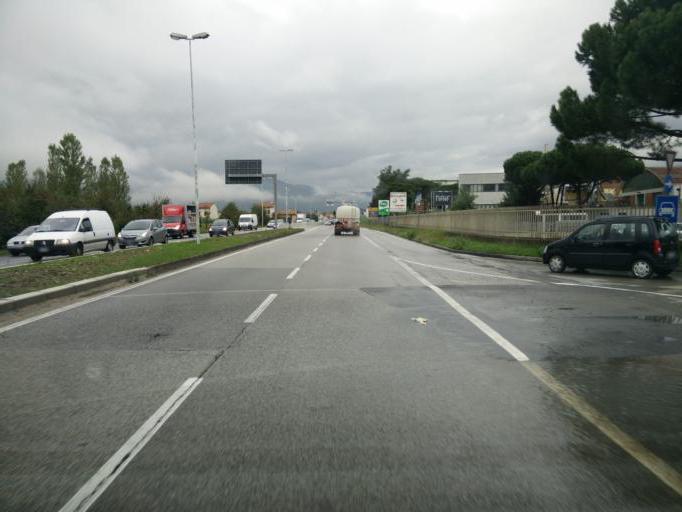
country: IT
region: Tuscany
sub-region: Provincia di Prato
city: Prato
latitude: 43.8808
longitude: 11.0646
